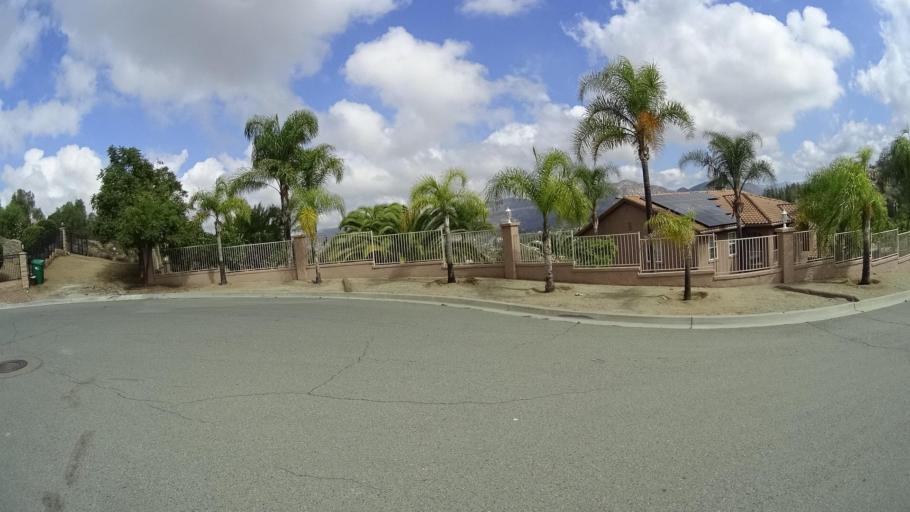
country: US
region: California
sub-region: San Diego County
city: Granite Hills
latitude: 32.7763
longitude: -116.9090
